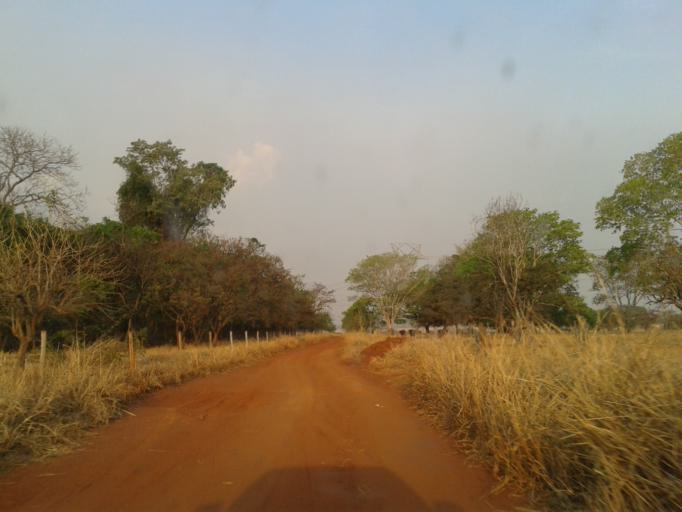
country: BR
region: Minas Gerais
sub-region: Capinopolis
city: Capinopolis
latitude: -18.8067
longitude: -49.7435
